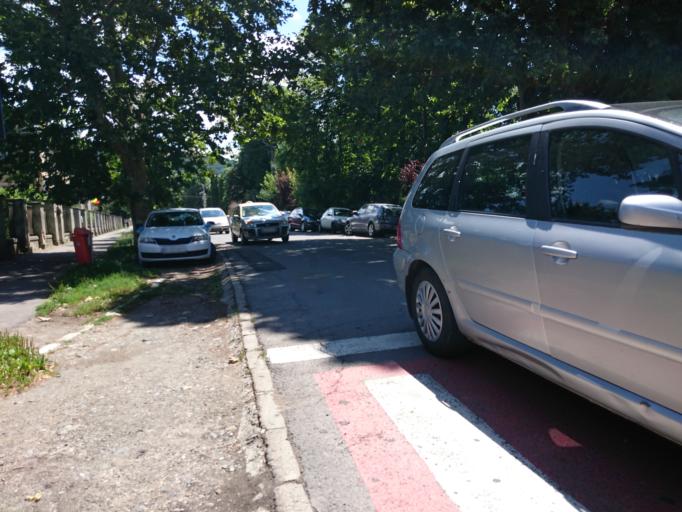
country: RO
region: Mures
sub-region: Municipiul Sighisoara
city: Sighisoara
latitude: 46.2224
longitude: 24.7958
